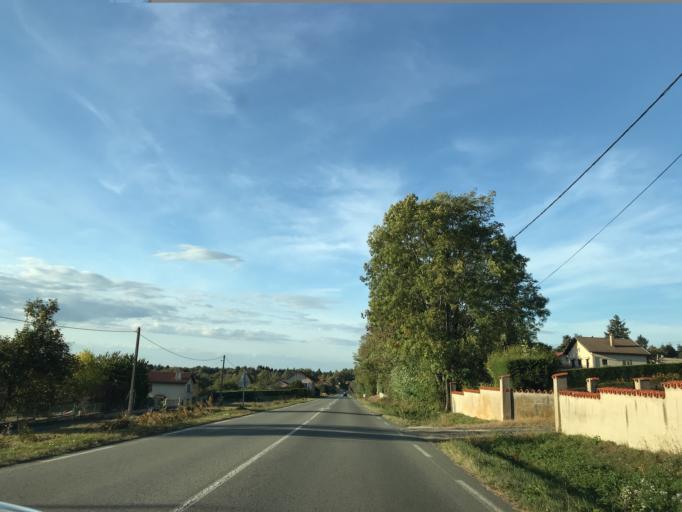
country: FR
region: Auvergne
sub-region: Departement du Puy-de-Dome
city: Paslieres
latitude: 45.9294
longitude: 3.4978
